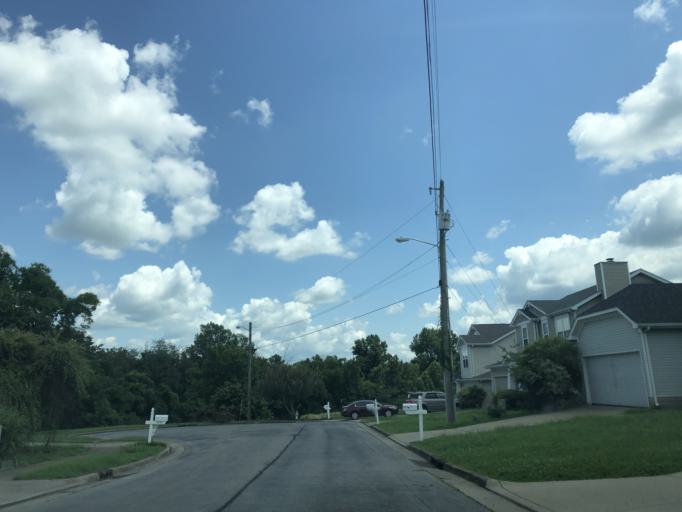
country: US
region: Tennessee
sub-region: Wilson County
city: Green Hill
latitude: 36.2215
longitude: -86.5923
